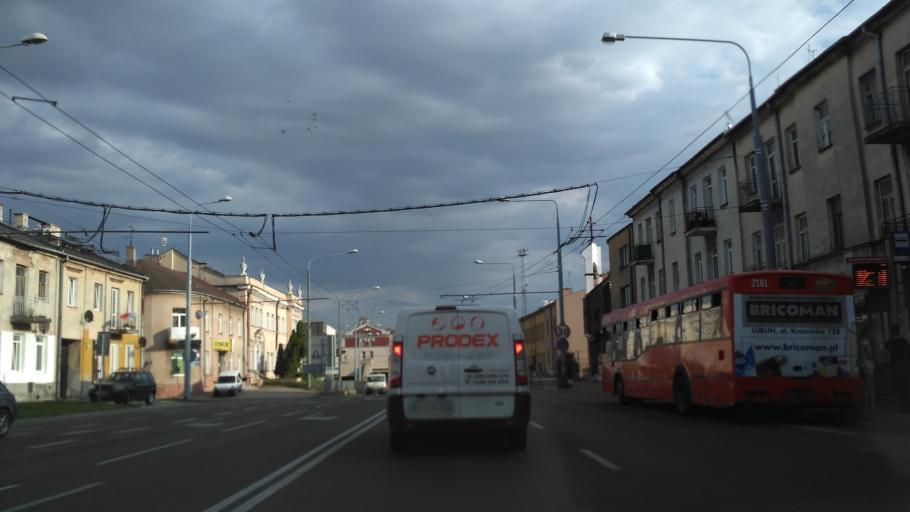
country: PL
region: Lublin Voivodeship
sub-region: Powiat lubelski
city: Lublin
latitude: 51.2341
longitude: 22.5709
